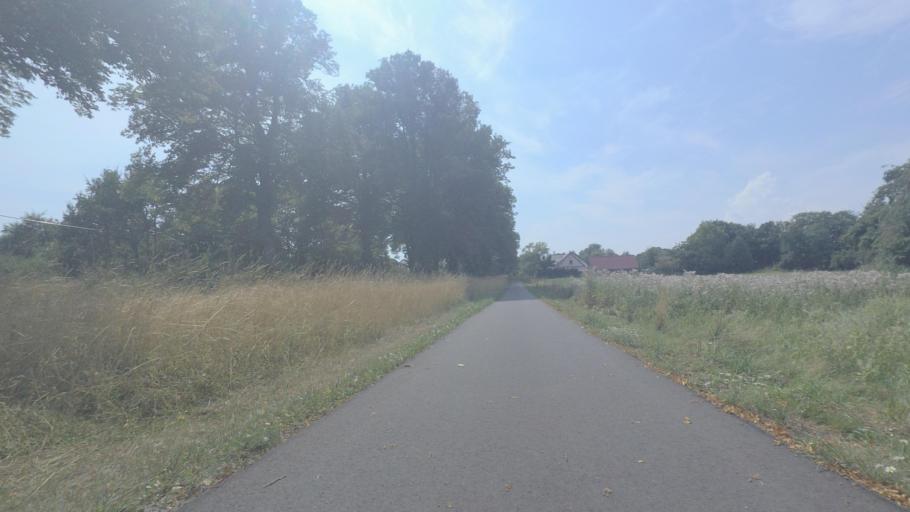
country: DE
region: Mecklenburg-Vorpommern
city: Garz
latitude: 54.2500
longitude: 13.3444
